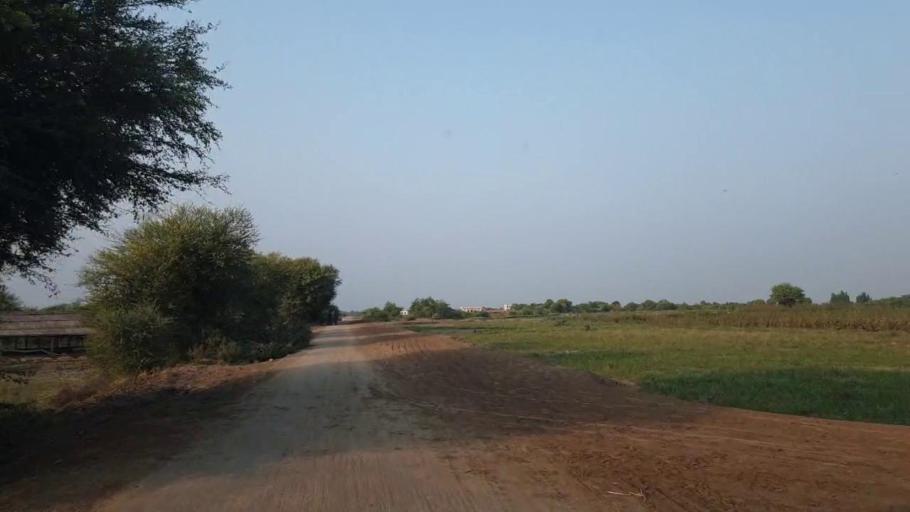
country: PK
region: Sindh
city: Rajo Khanani
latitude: 25.0467
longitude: 68.9644
